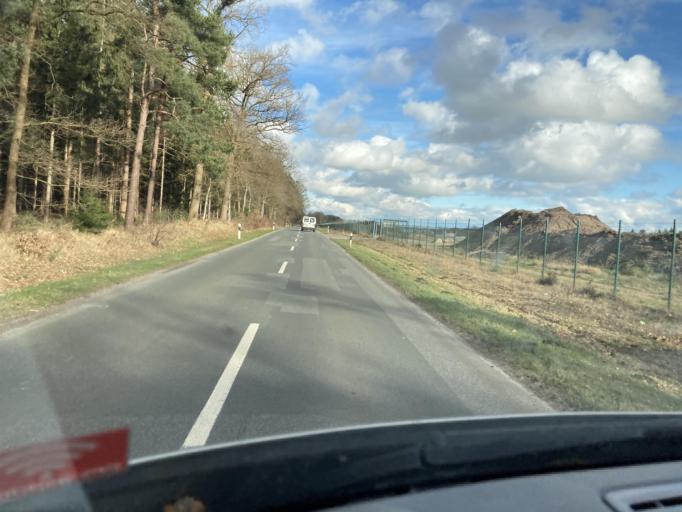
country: DE
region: Lower Saxony
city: Friedeburg
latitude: 53.4028
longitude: 7.8819
